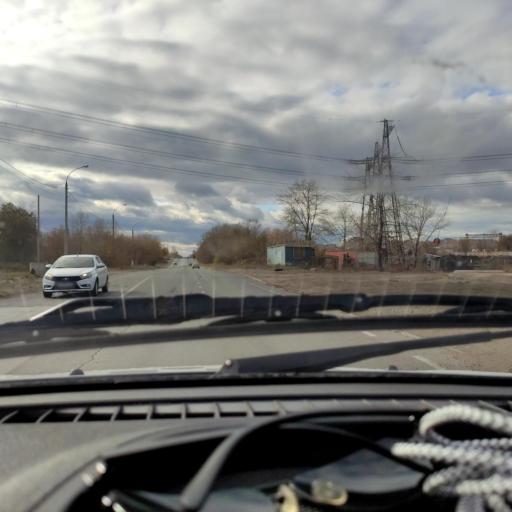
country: RU
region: Samara
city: Zhigulevsk
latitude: 53.4827
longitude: 49.5052
